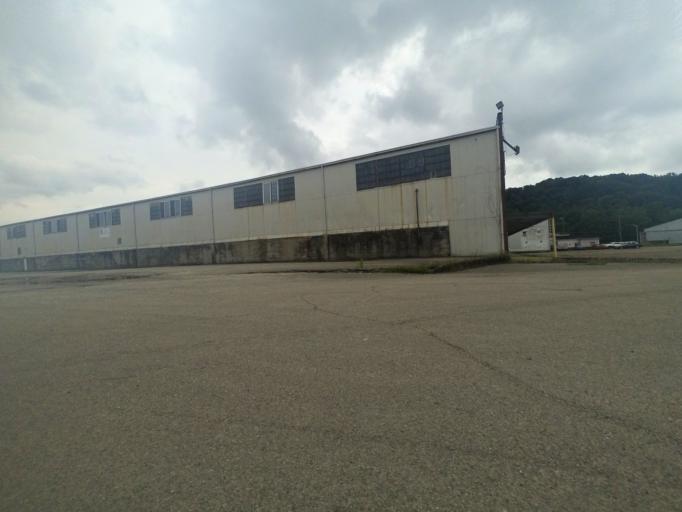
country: US
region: West Virginia
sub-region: Cabell County
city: Huntington
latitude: 38.4090
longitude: -82.4661
